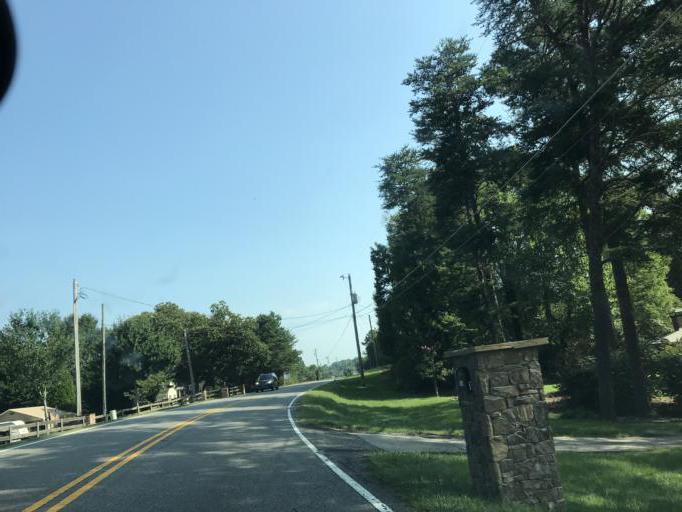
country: US
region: Georgia
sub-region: Forsyth County
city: Cumming
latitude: 34.2416
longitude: -84.1707
